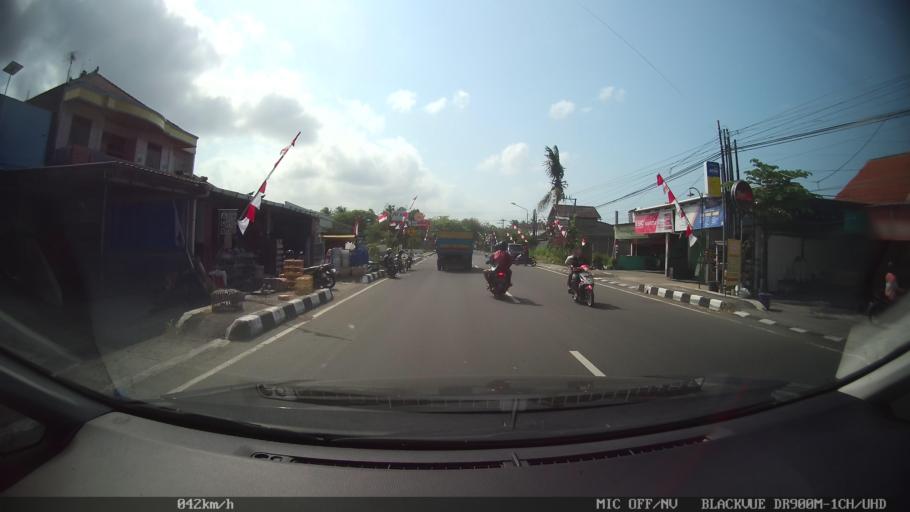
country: ID
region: Daerah Istimewa Yogyakarta
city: Srandakan
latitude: -7.8952
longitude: 110.1512
